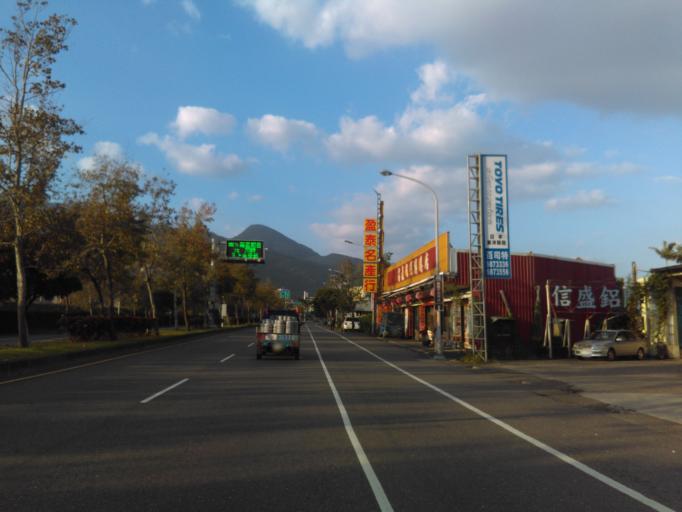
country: TW
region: Taiwan
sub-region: Yilan
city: Yilan
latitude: 24.8133
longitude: 121.7675
